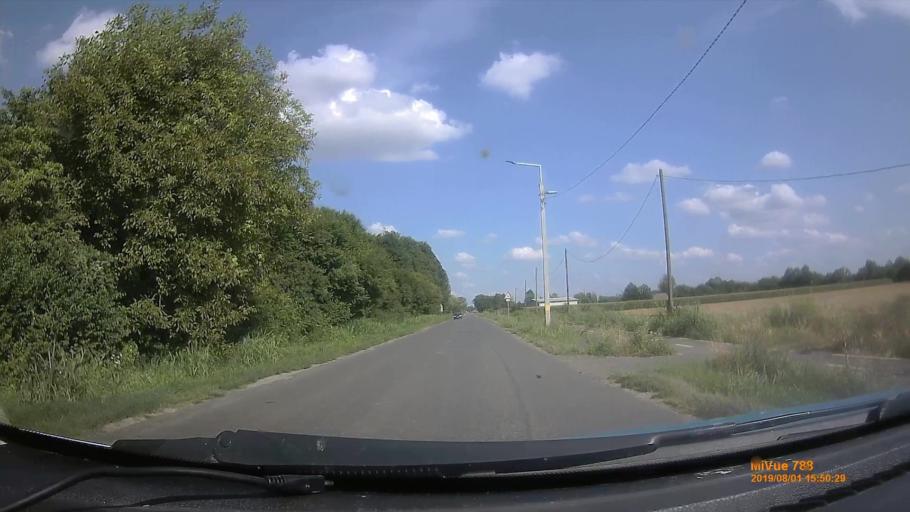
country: HU
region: Baranya
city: Szentlorinc
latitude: 46.0370
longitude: 18.0002
